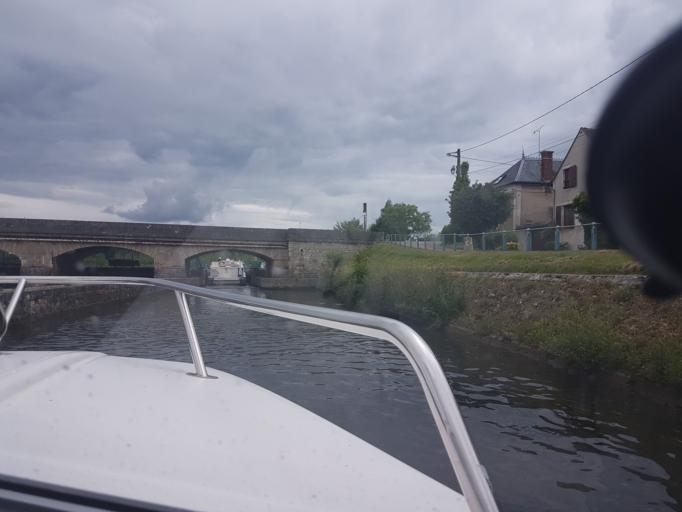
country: FR
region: Bourgogne
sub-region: Departement de l'Yonne
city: Champs-sur-Yonne
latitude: 47.7328
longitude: 3.6002
